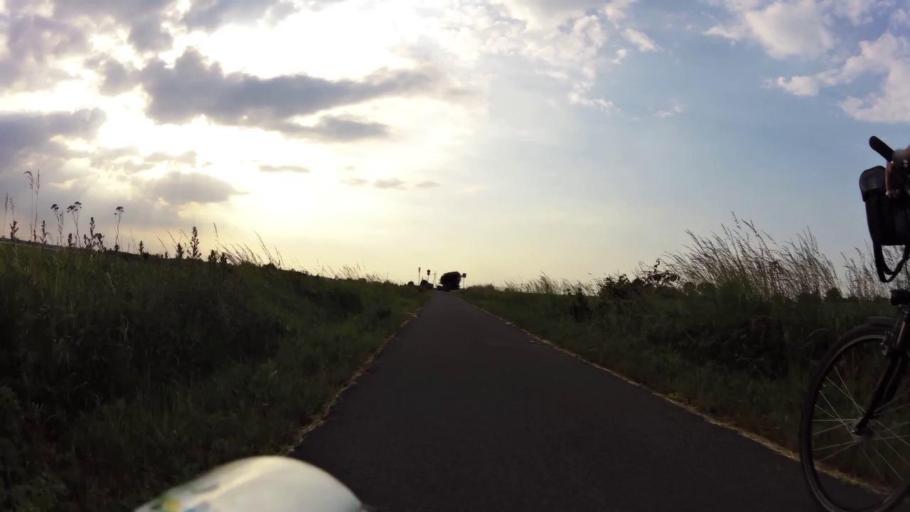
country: PL
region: Kujawsko-Pomorskie
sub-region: Powiat chelminski
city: Unislaw
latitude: 53.1767
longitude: 18.4128
